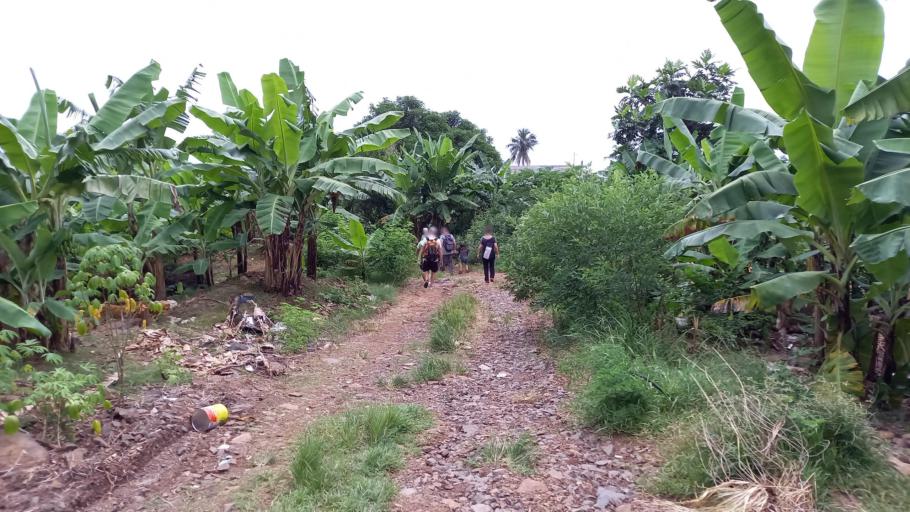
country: YT
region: Acoua
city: Acoua
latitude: -12.7148
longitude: 45.0525
